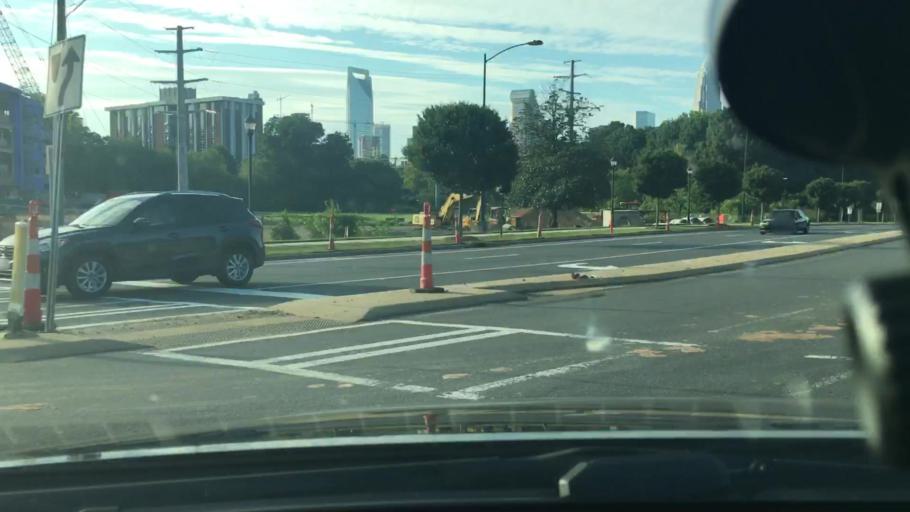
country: US
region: North Carolina
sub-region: Mecklenburg County
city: Charlotte
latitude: 35.2107
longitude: -80.8371
